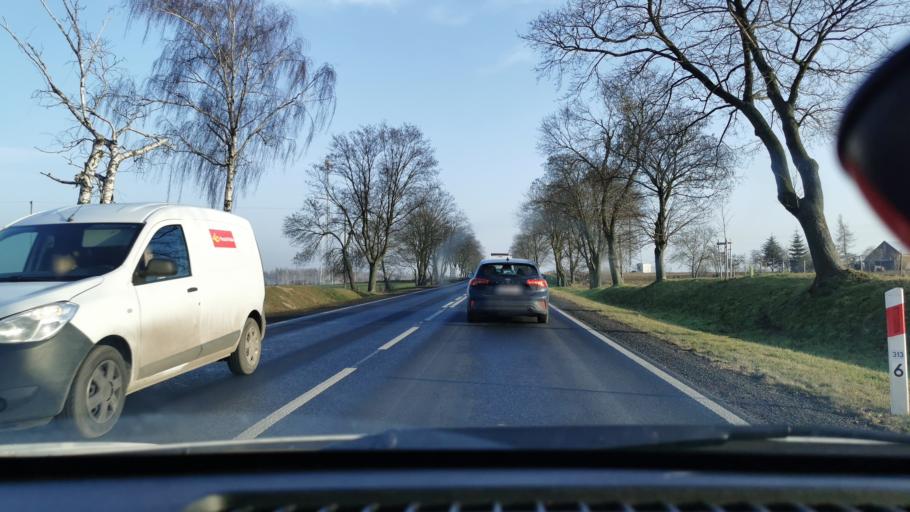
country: PL
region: Lodz Voivodeship
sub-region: Powiat sieradzki
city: Wroblew
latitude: 51.6180
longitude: 18.5941
